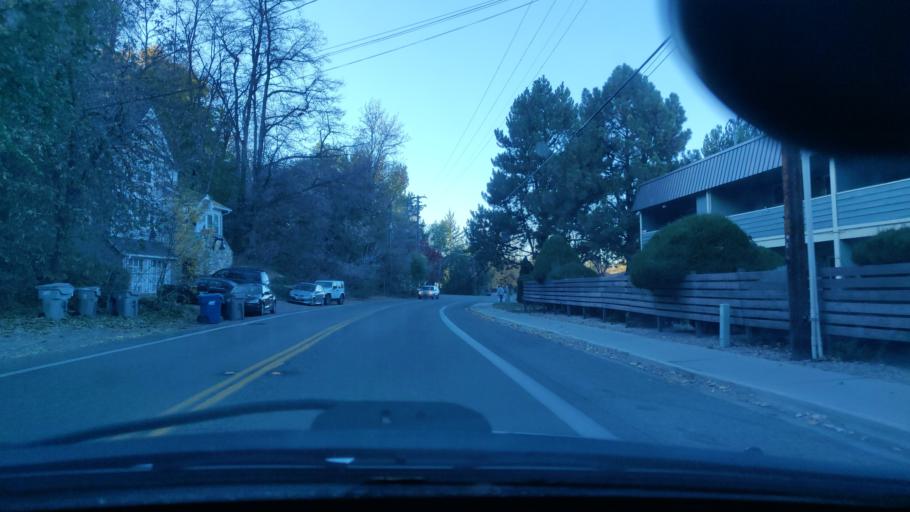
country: US
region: Idaho
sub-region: Ada County
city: Boise
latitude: 43.6017
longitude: -116.2102
